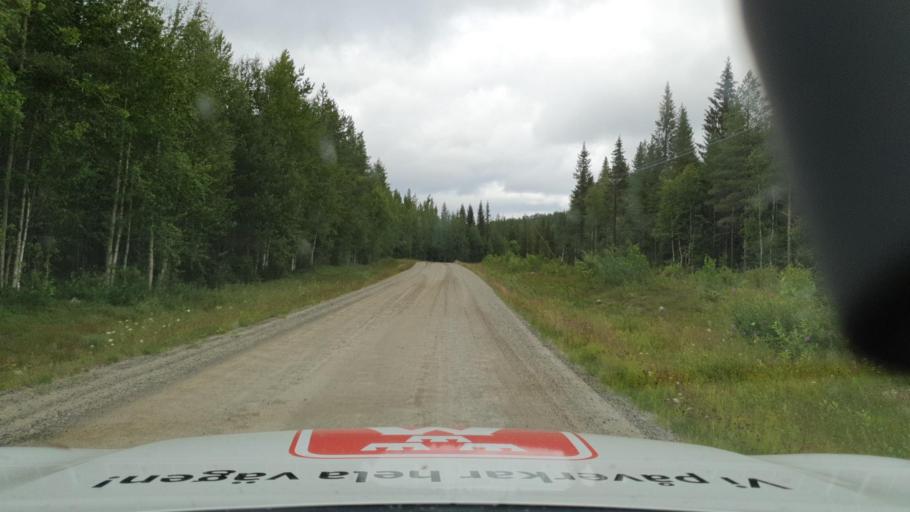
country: SE
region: Vaesterbotten
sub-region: Dorotea Kommun
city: Dorotea
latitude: 64.2004
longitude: 16.6869
